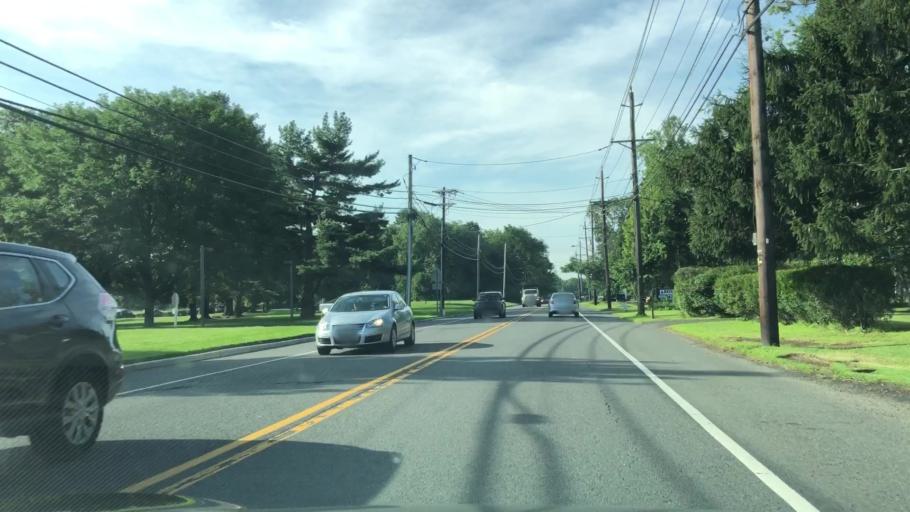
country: US
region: New Jersey
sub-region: Mercer County
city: Pennington
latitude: 40.3454
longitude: -74.7965
